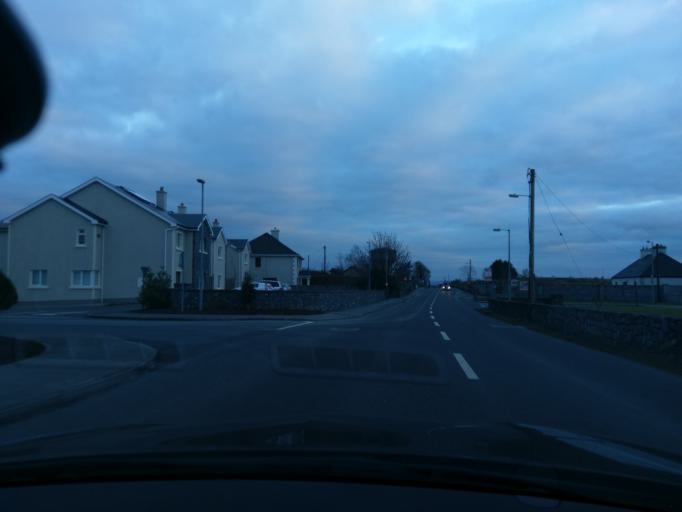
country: IE
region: Connaught
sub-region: County Galway
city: Athenry
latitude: 53.3075
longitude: -8.7525
